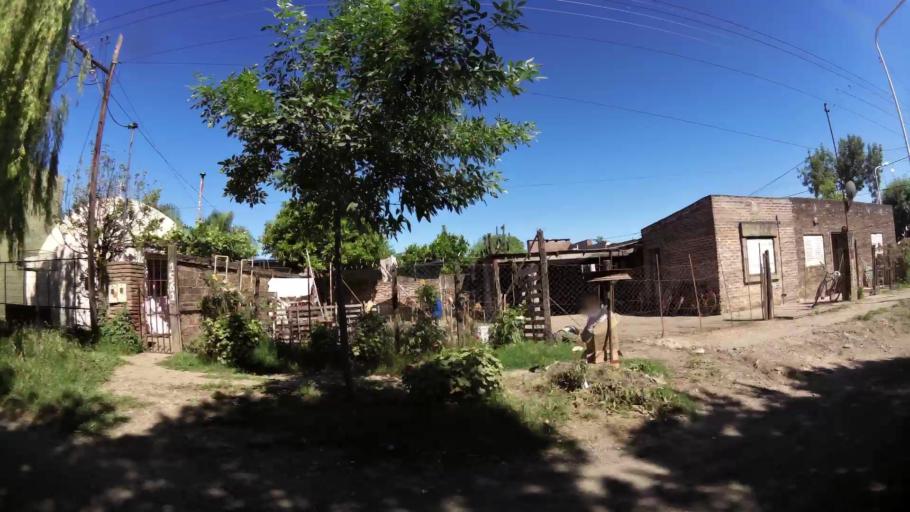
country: AR
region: Santa Fe
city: Esperanza
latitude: -31.4511
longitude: -60.9418
